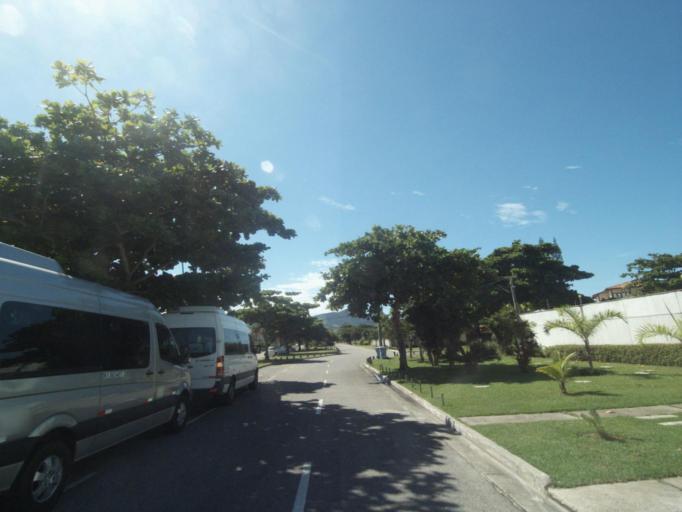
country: BR
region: Rio de Janeiro
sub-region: Niteroi
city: Niteroi
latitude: -22.9581
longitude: -43.0621
